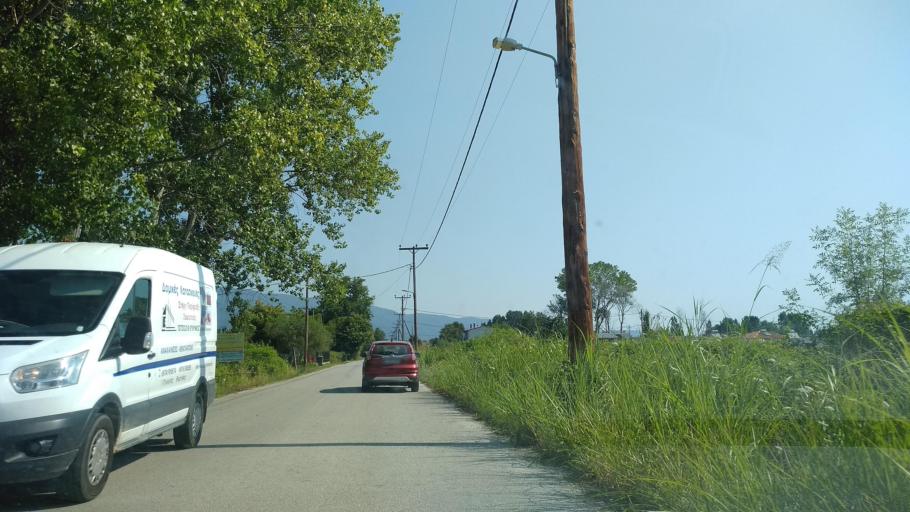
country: GR
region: Central Macedonia
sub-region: Nomos Thessalonikis
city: Stavros
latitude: 40.6809
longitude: 23.6871
